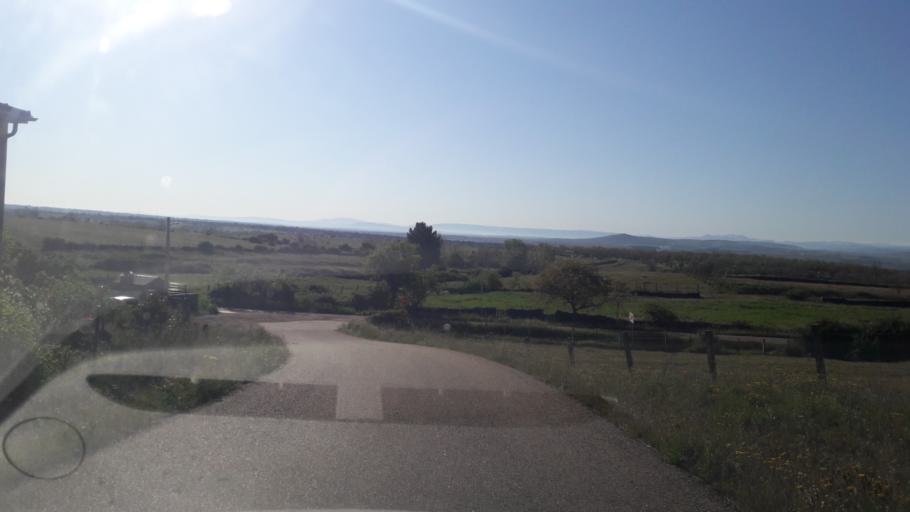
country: ES
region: Castille and Leon
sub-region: Provincia de Salamanca
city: Herguijuela del Campo
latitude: 40.6292
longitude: -5.8641
